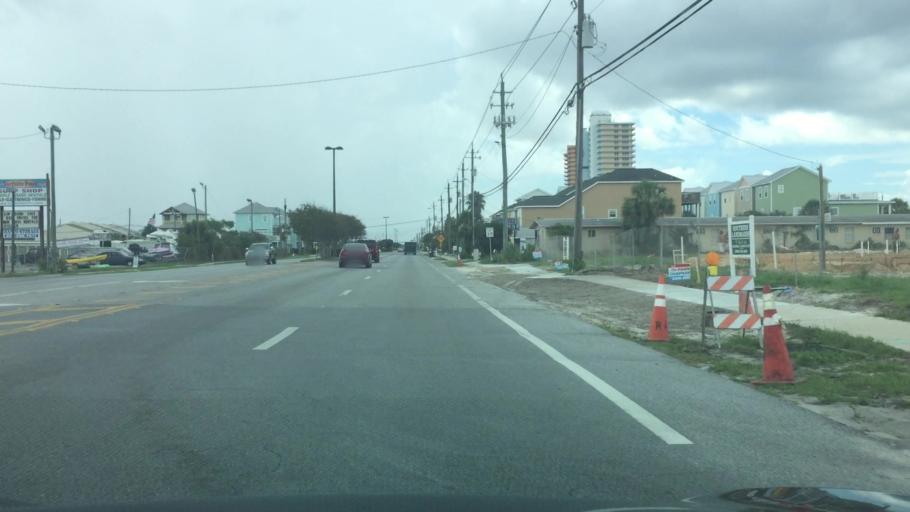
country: US
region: Florida
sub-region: Bay County
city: Lower Grand Lagoon
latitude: 30.1448
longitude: -85.7573
